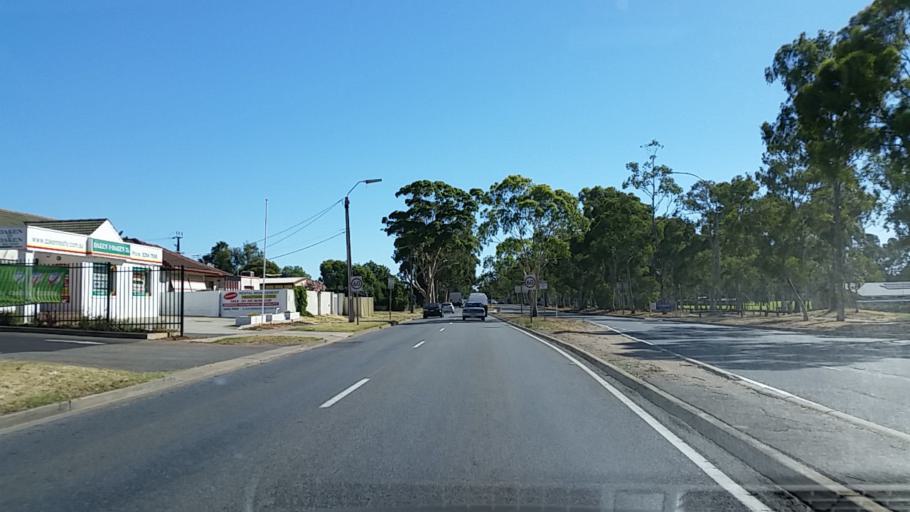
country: AU
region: South Australia
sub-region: Salisbury
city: Ingle Farm
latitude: -34.8071
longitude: 138.6489
